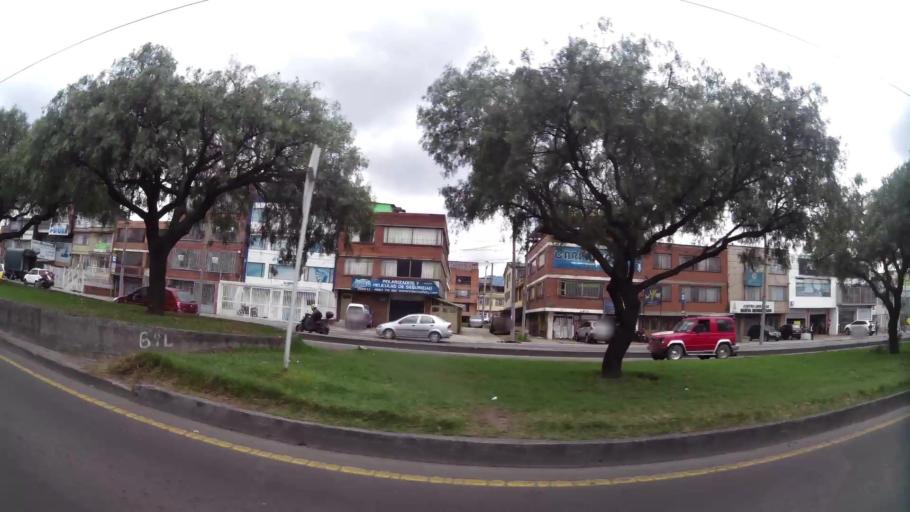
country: CO
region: Bogota D.C.
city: Barrio San Luis
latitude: 4.6759
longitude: -74.0870
